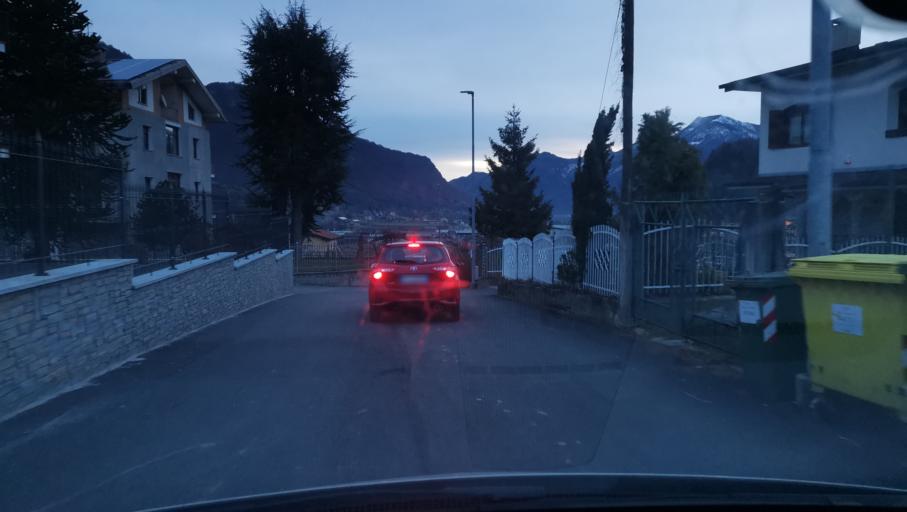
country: IT
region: Piedmont
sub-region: Provincia di Cuneo
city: Demonte
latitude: 44.3175
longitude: 7.2981
